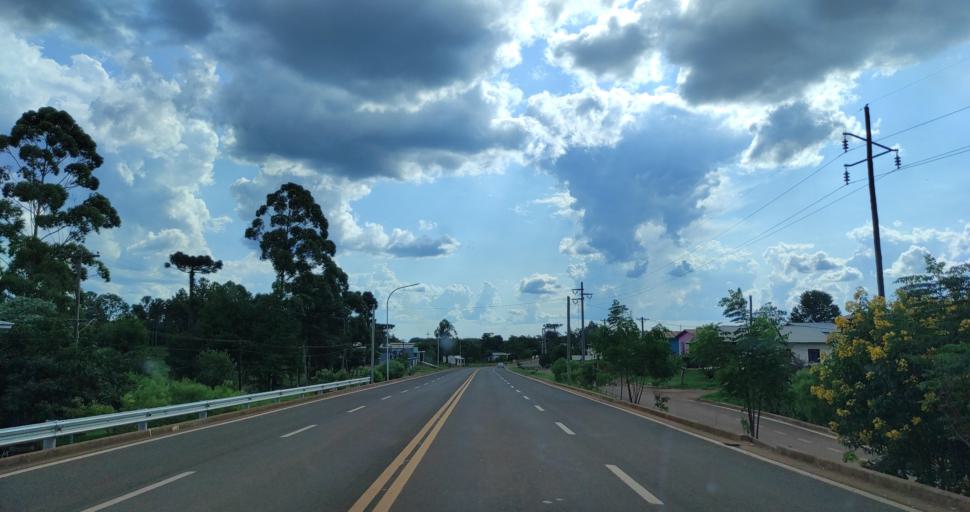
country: AR
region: Misiones
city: Bernardo de Irigoyen
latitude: -26.2947
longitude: -53.7467
